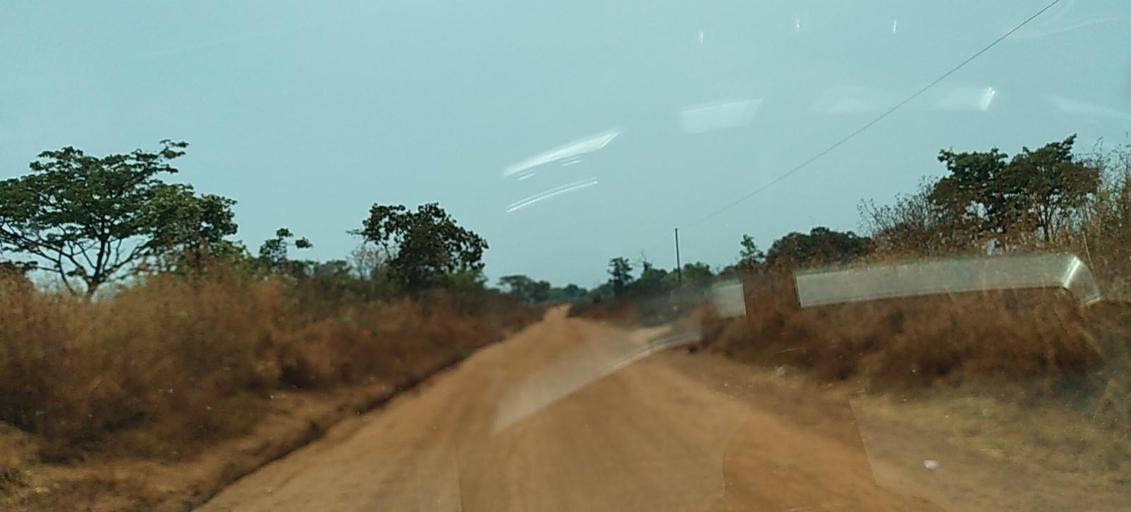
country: CD
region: Katanga
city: Kipushi
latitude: -11.9373
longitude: 26.9561
